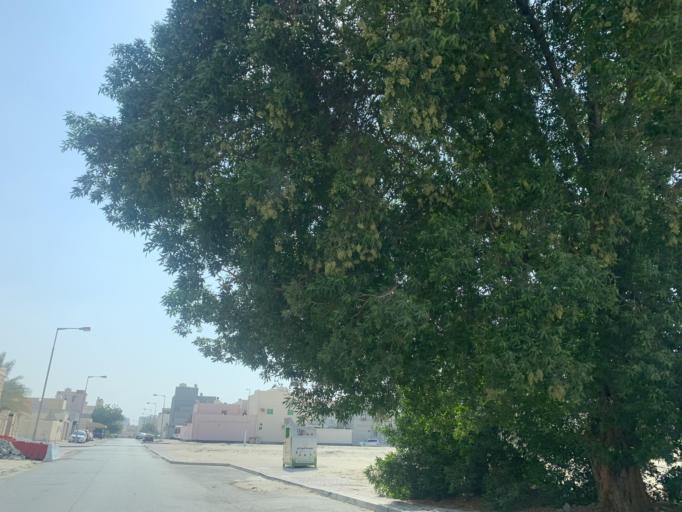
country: BH
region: Central Governorate
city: Madinat Hamad
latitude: 26.1229
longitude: 50.4908
